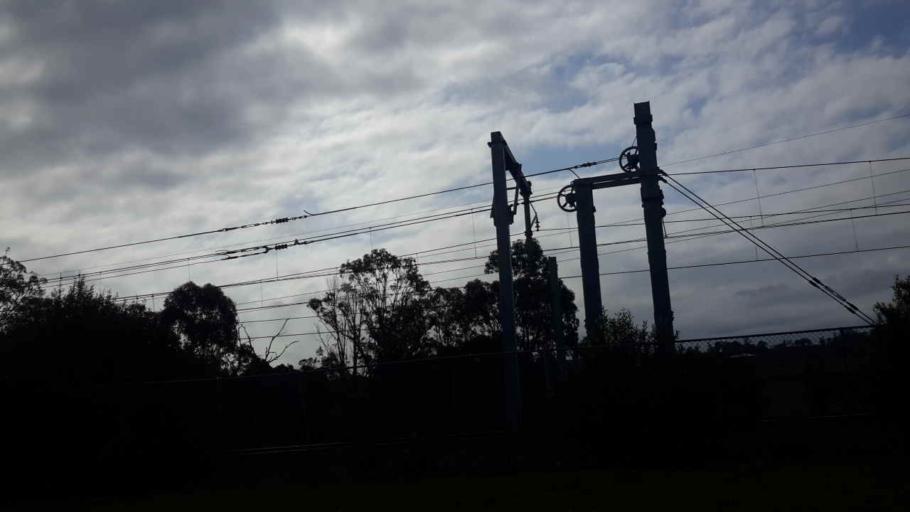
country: AU
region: New South Wales
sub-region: Campbelltown Municipality
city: Glen Alpine
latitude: -34.0784
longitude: 150.7836
